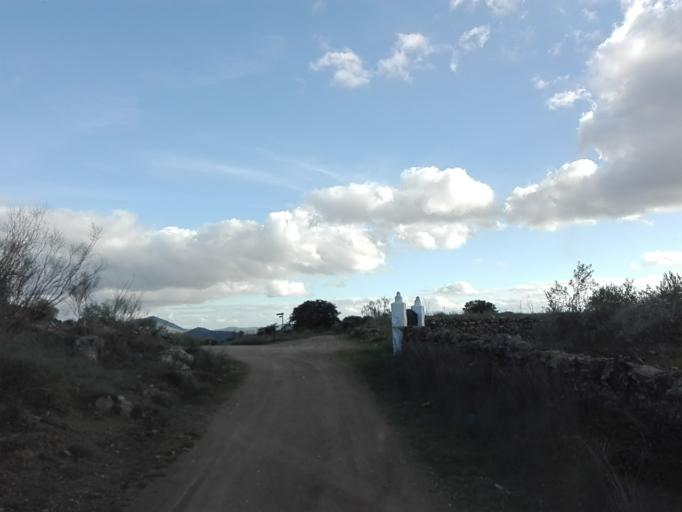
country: ES
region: Extremadura
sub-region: Provincia de Badajoz
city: Trasierra
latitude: 38.1850
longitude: -5.9863
